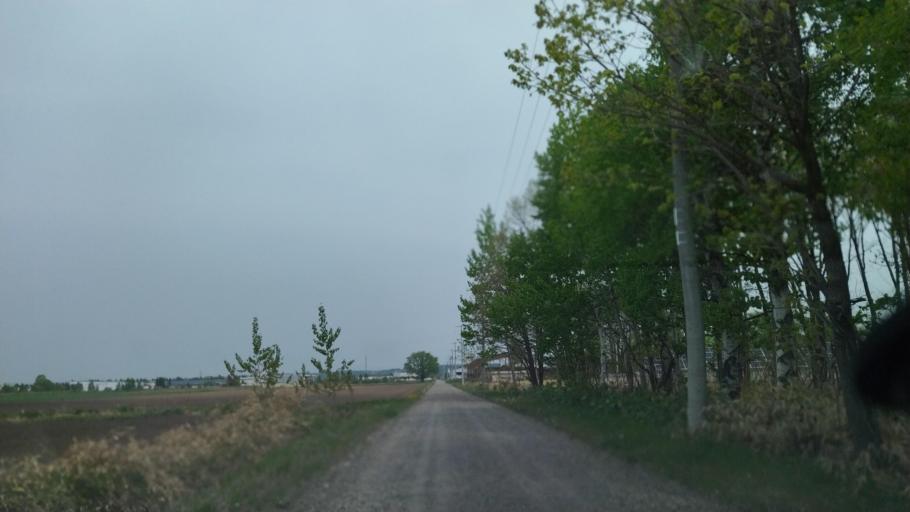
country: JP
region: Hokkaido
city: Obihiro
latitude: 42.9164
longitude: 143.0968
